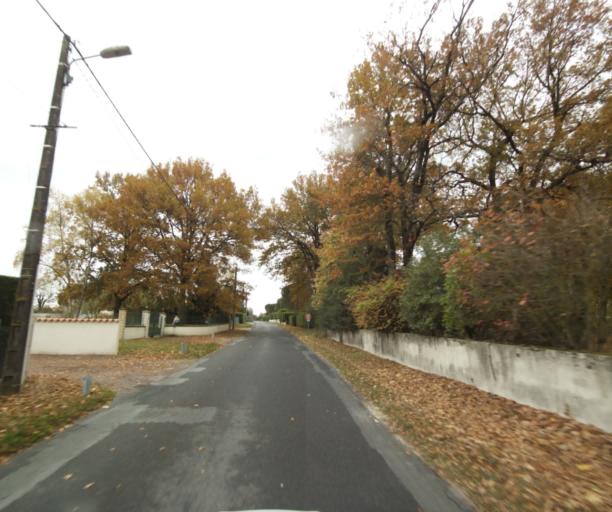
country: FR
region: Poitou-Charentes
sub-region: Departement de la Charente-Maritime
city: Fontcouverte
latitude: 45.7609
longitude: -0.5847
